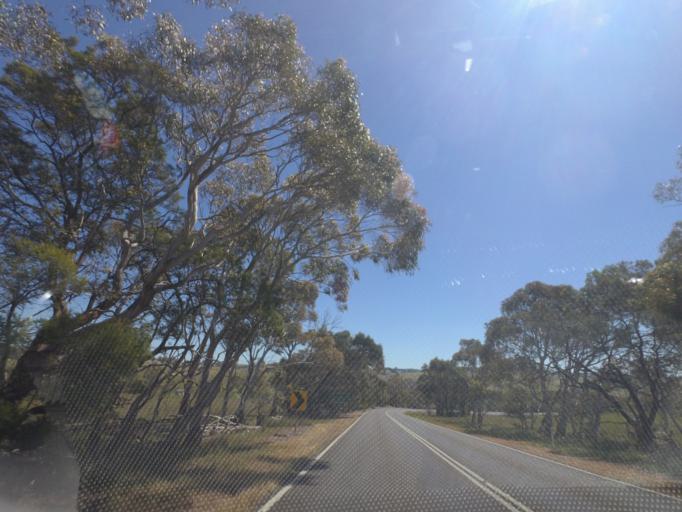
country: AU
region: Victoria
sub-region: Hume
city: Sunbury
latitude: -37.1200
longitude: 144.7628
